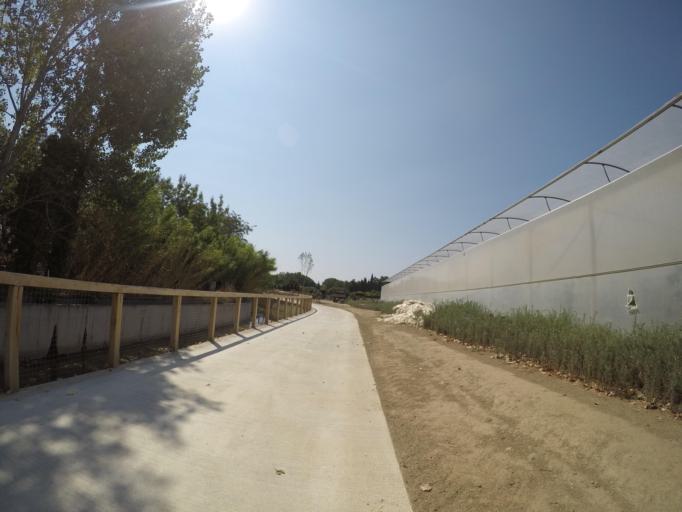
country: FR
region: Languedoc-Roussillon
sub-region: Departement des Pyrenees-Orientales
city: Saint-Esteve
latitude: 42.7027
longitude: 2.8552
